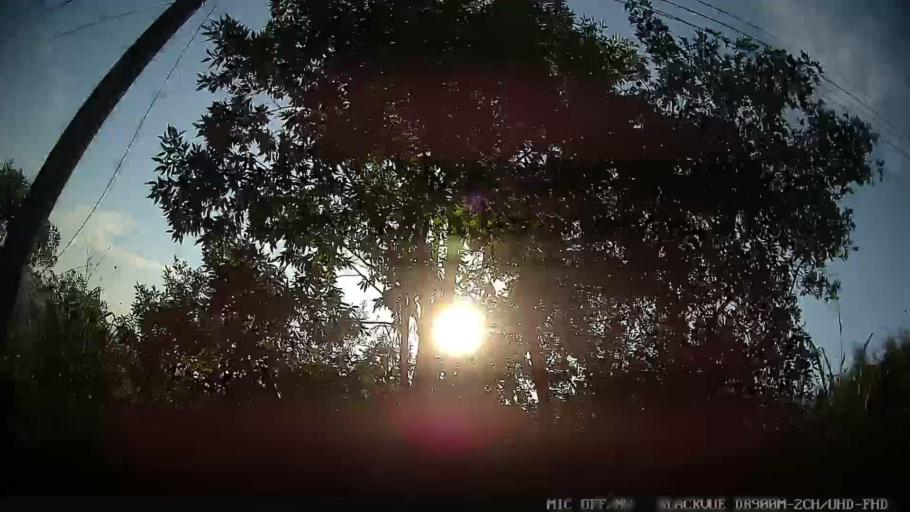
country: BR
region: Sao Paulo
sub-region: Guaruja
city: Guaruja
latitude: -23.9849
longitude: -46.2607
